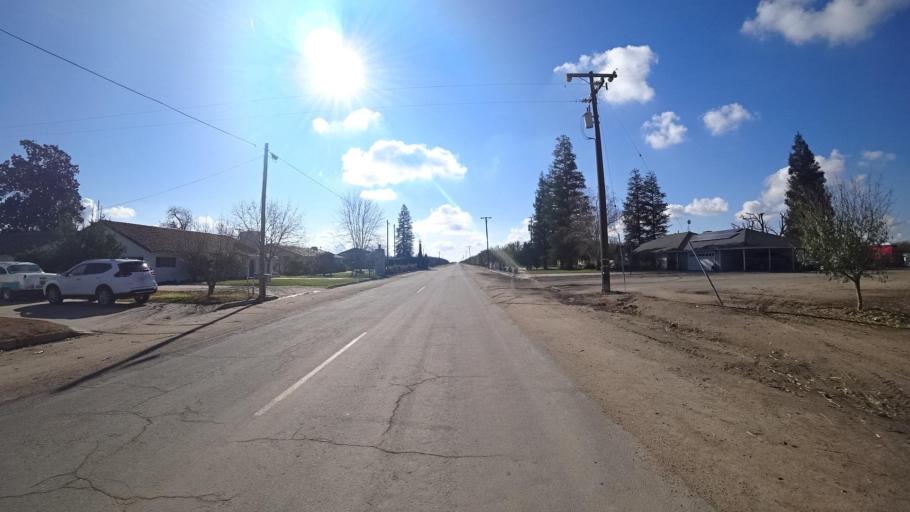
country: US
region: California
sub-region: Kern County
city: McFarland
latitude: 35.6969
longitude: -119.2583
